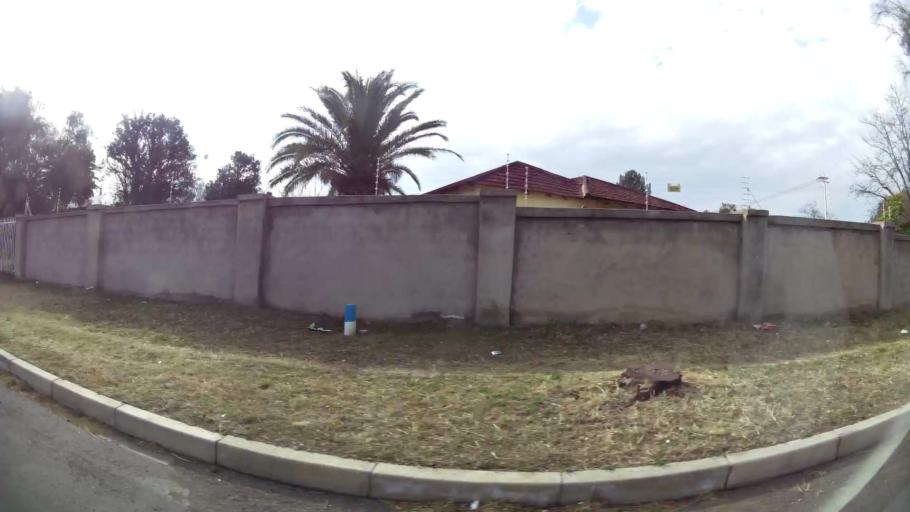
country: ZA
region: Orange Free State
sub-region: Mangaung Metropolitan Municipality
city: Bloemfontein
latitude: -29.0917
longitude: 26.2509
